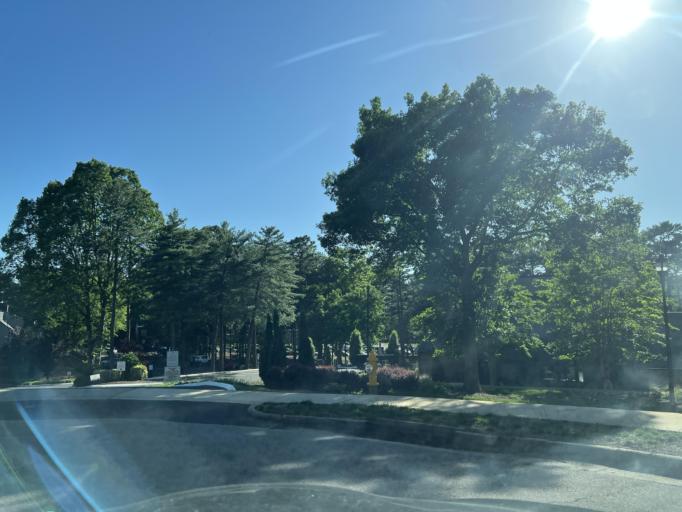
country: US
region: North Carolina
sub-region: Wake County
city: West Raleigh
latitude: 35.8582
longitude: -78.6428
